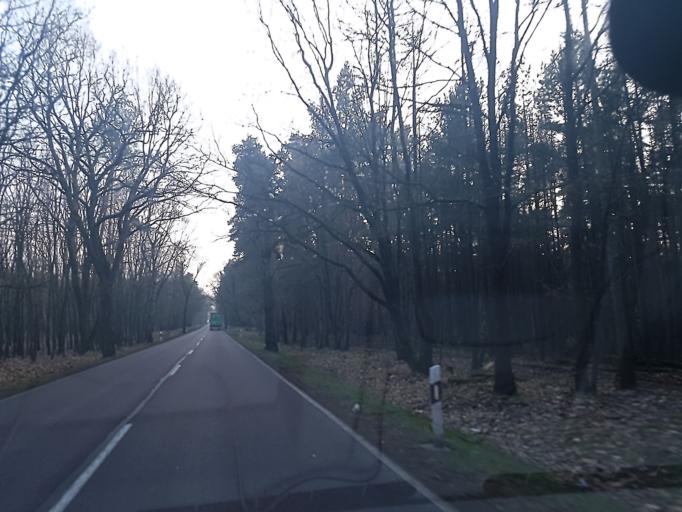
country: DE
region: Saxony-Anhalt
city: Coswig
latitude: 51.9727
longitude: 12.4661
